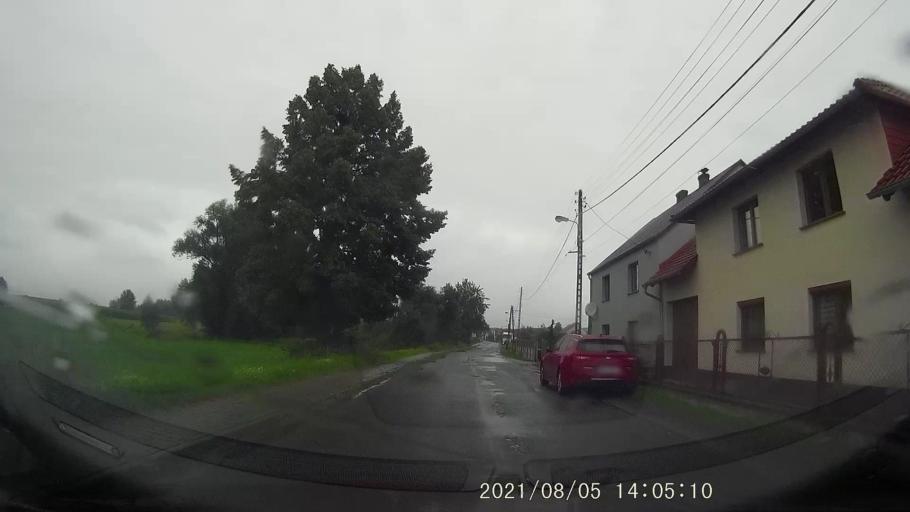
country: PL
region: Opole Voivodeship
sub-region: Powiat krapkowicki
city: Strzeleczki
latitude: 50.4632
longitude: 17.8552
